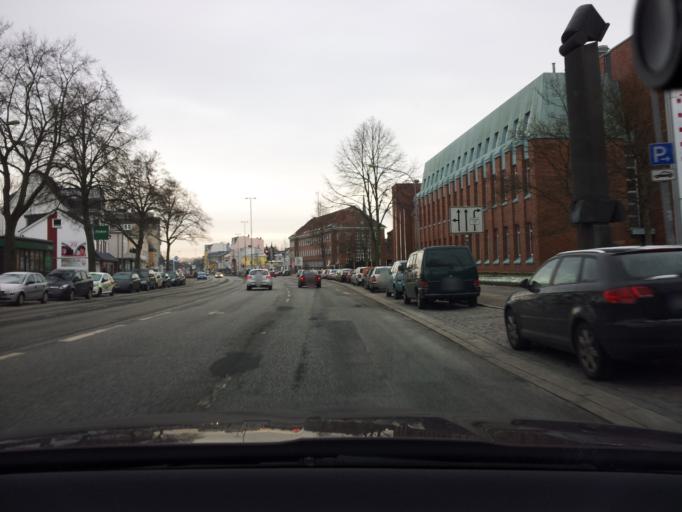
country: DE
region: Schleswig-Holstein
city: Luebeck
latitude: 53.8722
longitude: 10.6672
